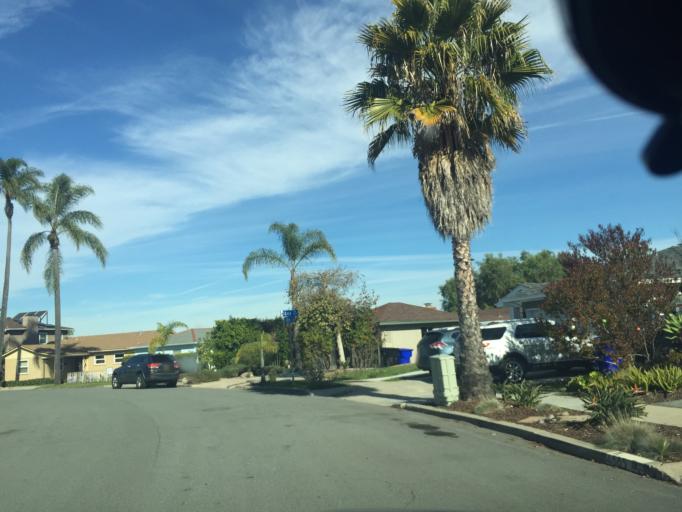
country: US
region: California
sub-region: San Diego County
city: Lemon Grove
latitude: 32.7670
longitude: -117.0889
